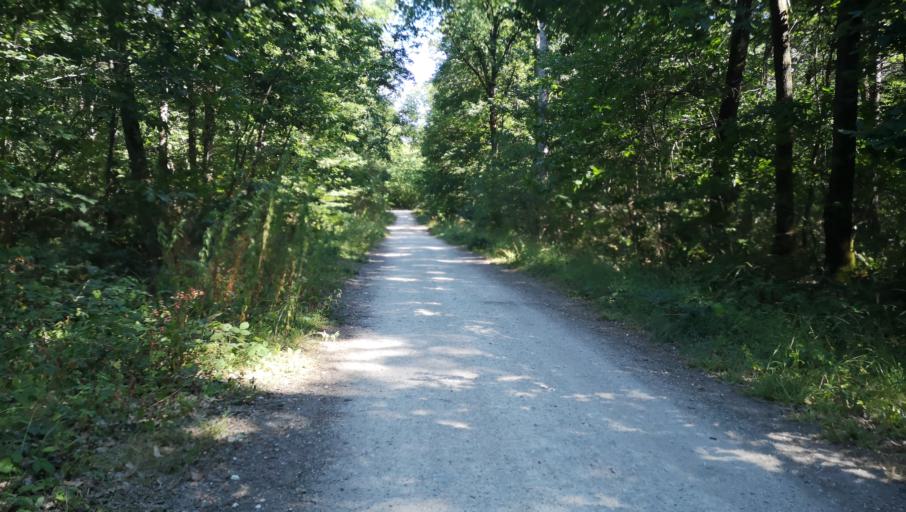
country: FR
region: Centre
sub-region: Departement du Loiret
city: Saint-Jean-de-Braye
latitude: 47.9383
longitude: 1.9806
